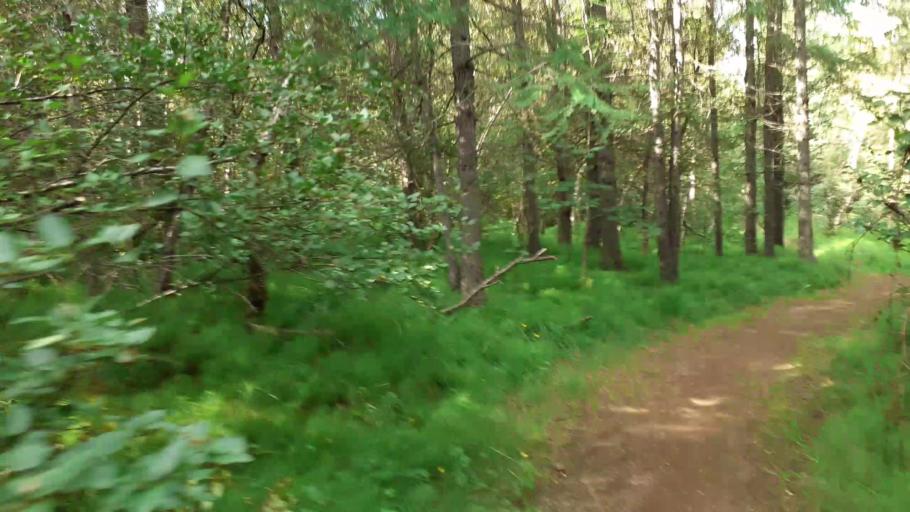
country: IS
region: Northeast
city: Akureyri
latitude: 65.6400
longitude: -18.0948
